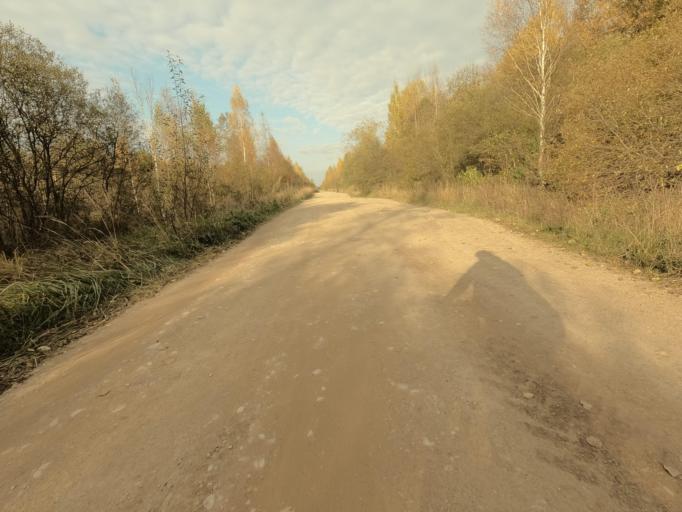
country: RU
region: Novgorod
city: Volkhovskiy
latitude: 58.9030
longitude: 31.0346
